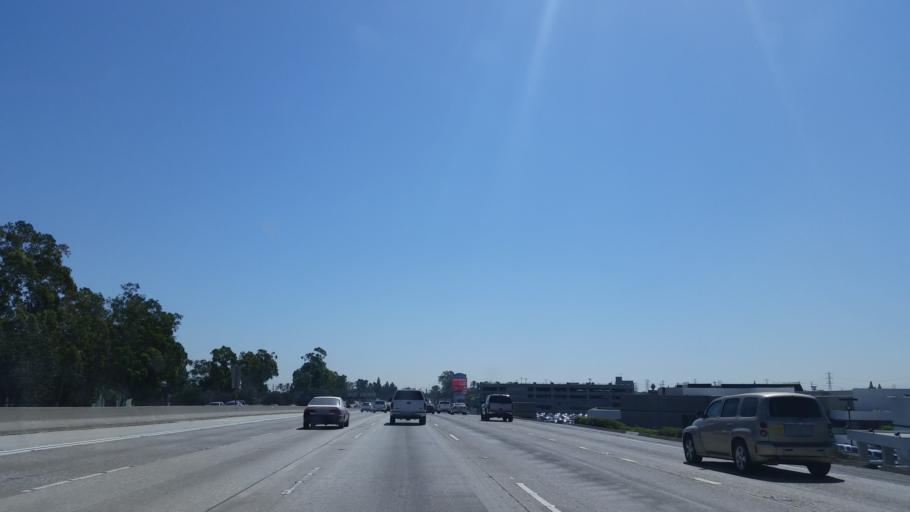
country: US
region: California
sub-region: Los Angeles County
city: Artesia
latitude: 33.8652
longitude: -118.0986
